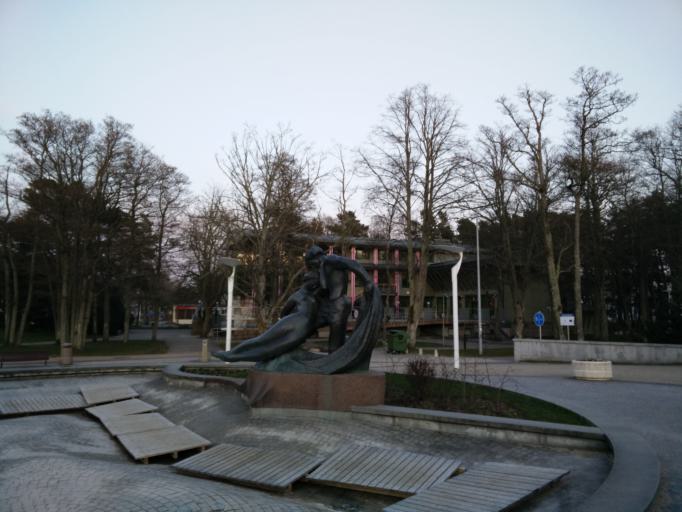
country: LT
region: Klaipedos apskritis
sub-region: Klaipeda
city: Palanga
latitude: 55.9196
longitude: 21.0520
